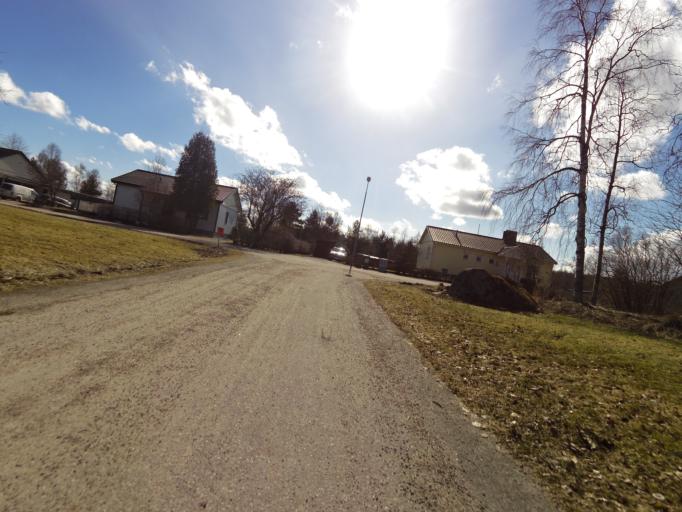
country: SE
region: Gaevleborg
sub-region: Hofors Kommun
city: Hofors
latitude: 60.5373
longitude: 16.3139
